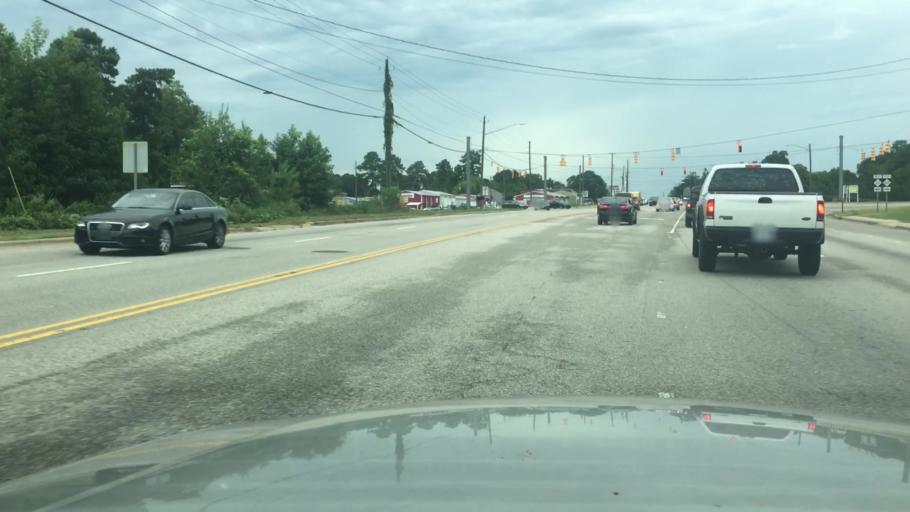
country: US
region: North Carolina
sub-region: Cumberland County
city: Hope Mills
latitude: 34.9942
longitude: -78.9678
